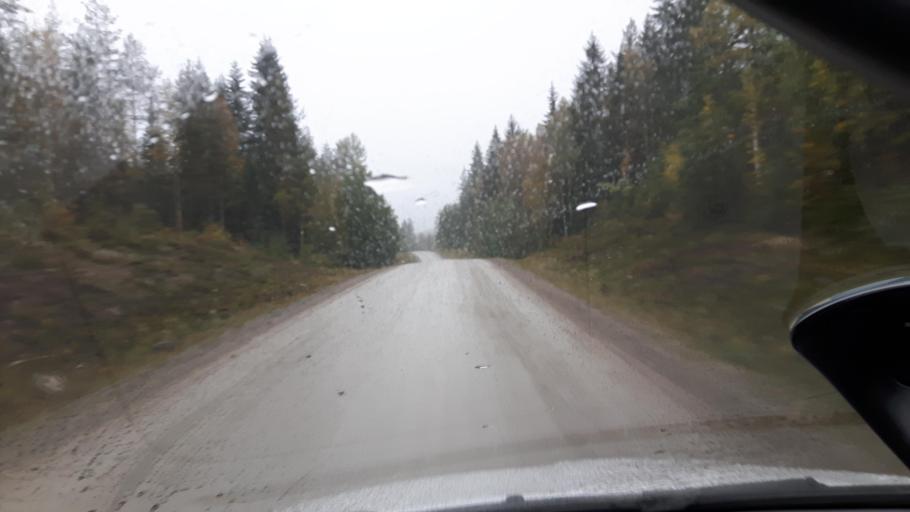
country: SE
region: Gaevleborg
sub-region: Ljusdals Kommun
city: Farila
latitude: 62.0302
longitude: 15.8220
